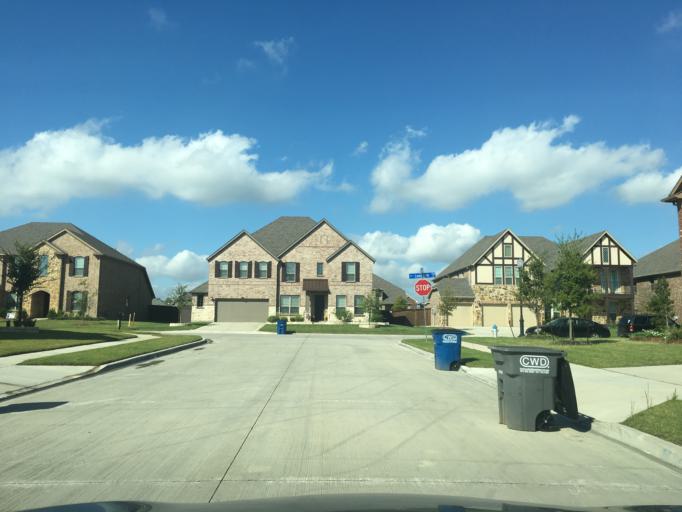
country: US
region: Texas
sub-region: Dallas County
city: Sachse
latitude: 32.9639
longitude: -96.5742
